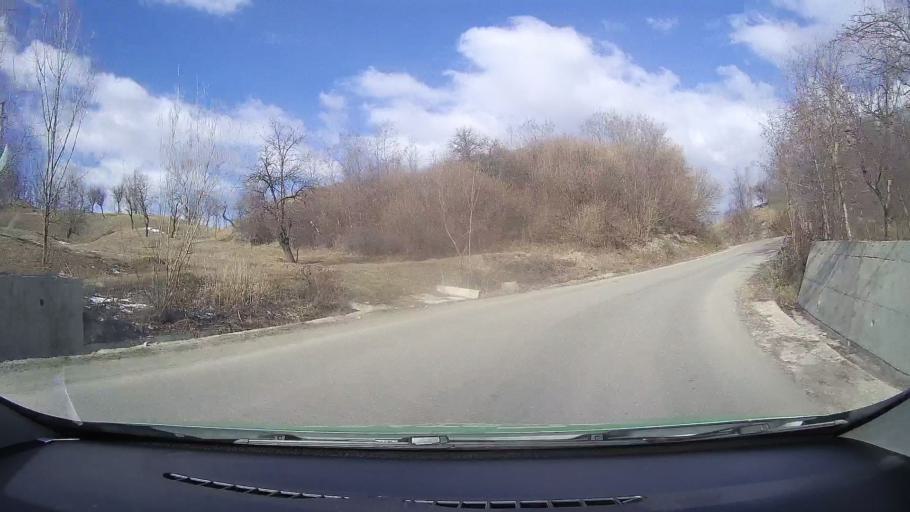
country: RO
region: Dambovita
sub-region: Oras Pucioasa
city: Glodeni
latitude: 45.0905
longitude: 25.4723
